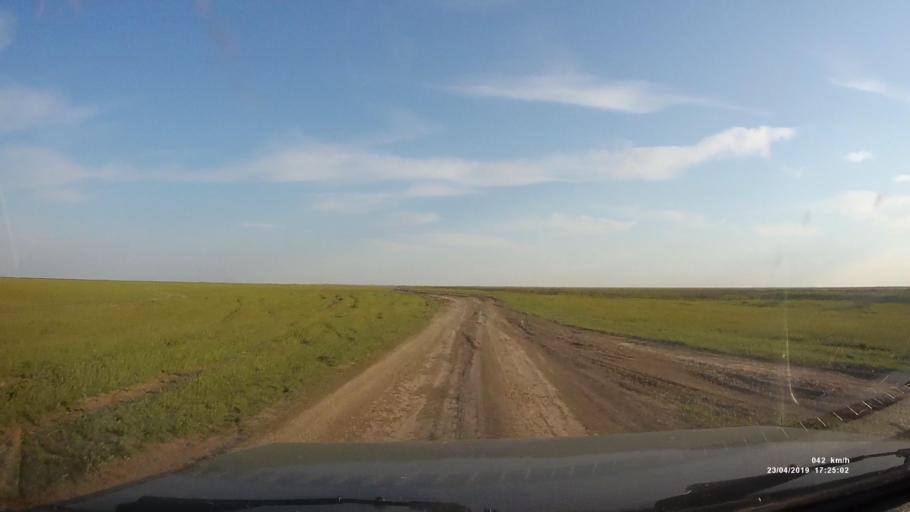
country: RU
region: Kalmykiya
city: Priyutnoye
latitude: 46.1541
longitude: 43.5097
